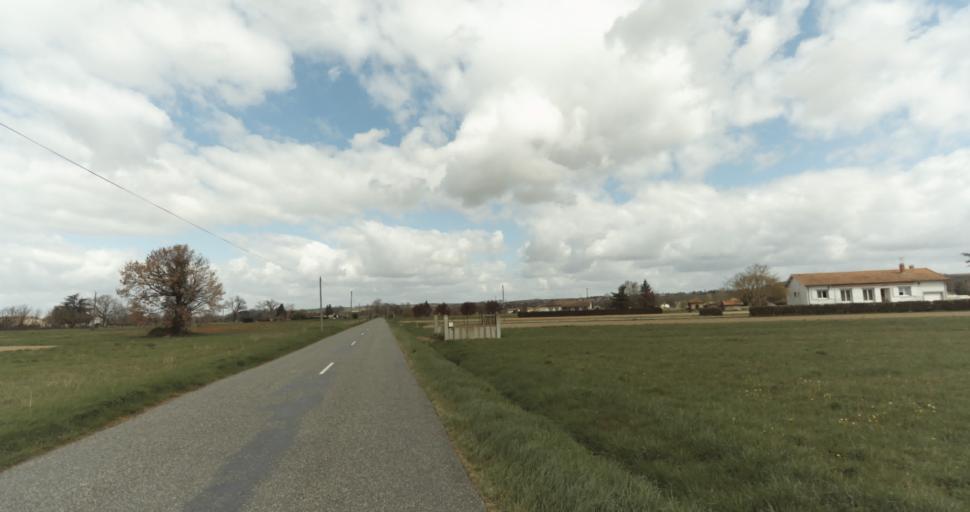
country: FR
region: Midi-Pyrenees
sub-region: Departement de la Haute-Garonne
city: Auterive
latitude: 43.3309
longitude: 1.4782
